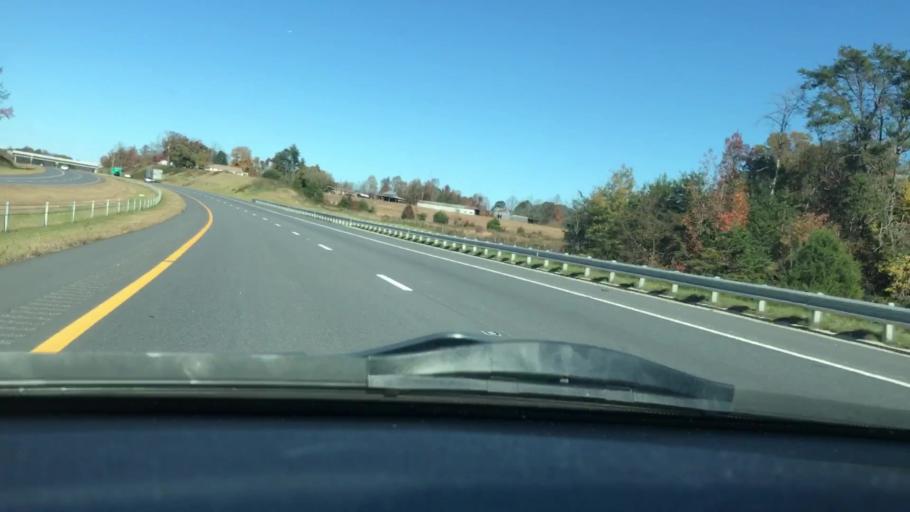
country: US
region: North Carolina
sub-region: Guilford County
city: Summerfield
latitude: 36.1793
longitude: -79.9329
